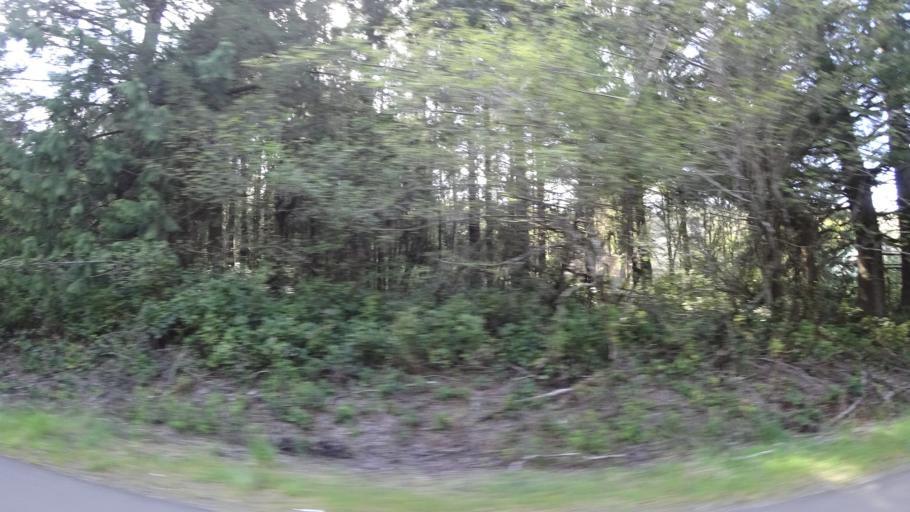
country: US
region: Oregon
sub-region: Lane County
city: Dunes City
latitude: 43.8975
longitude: -124.1173
